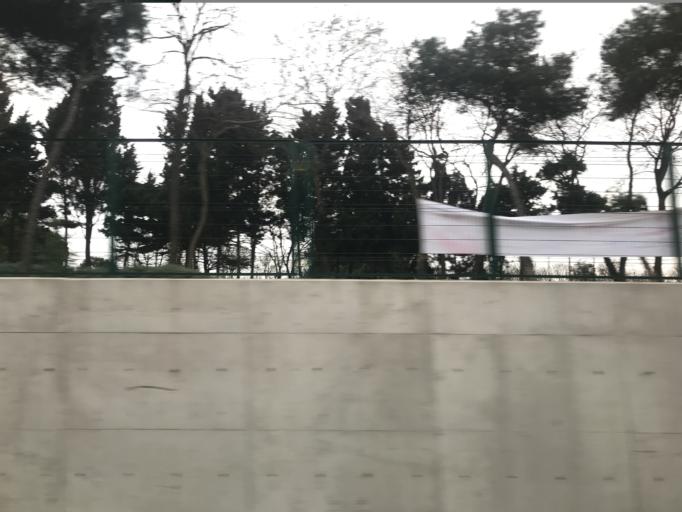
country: TR
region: Istanbul
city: Bahcelievler
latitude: 40.9710
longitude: 28.7922
